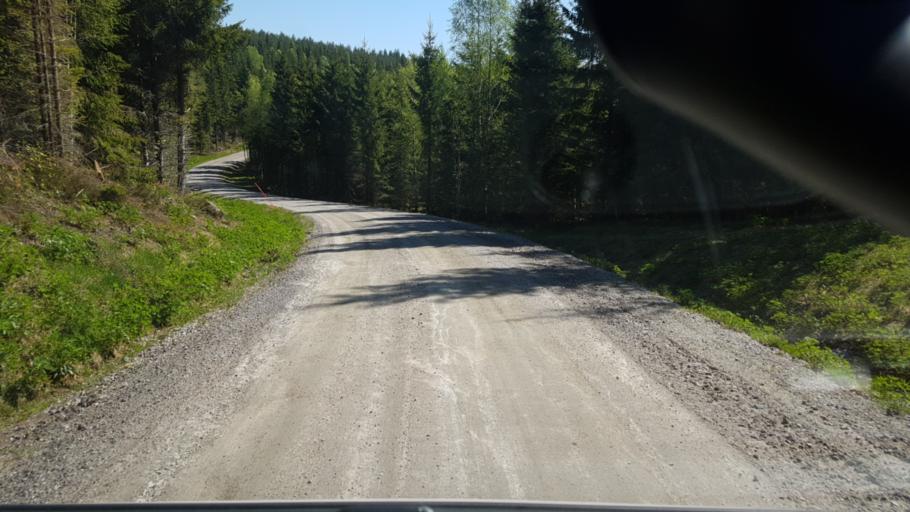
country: SE
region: Vaermland
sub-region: Arvika Kommun
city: Arvika
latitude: 59.8354
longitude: 12.8111
